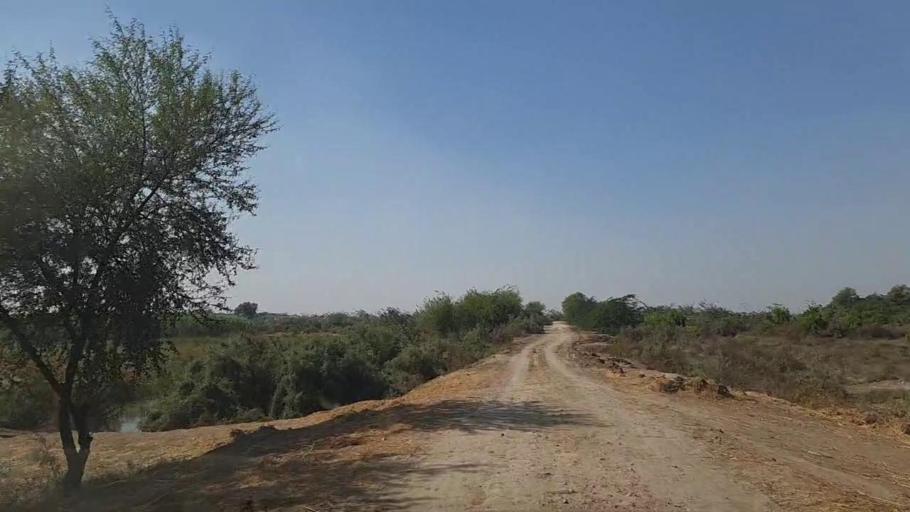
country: PK
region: Sindh
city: Daro Mehar
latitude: 24.8384
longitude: 68.1353
